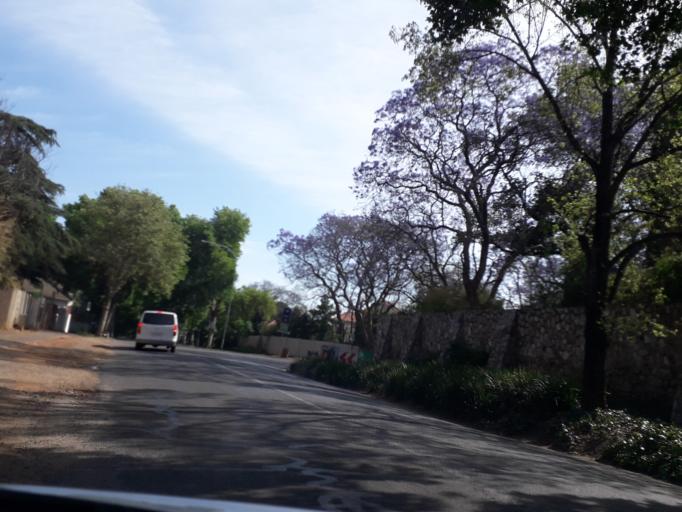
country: ZA
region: Gauteng
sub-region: City of Johannesburg Metropolitan Municipality
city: Johannesburg
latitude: -26.1648
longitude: 28.0428
